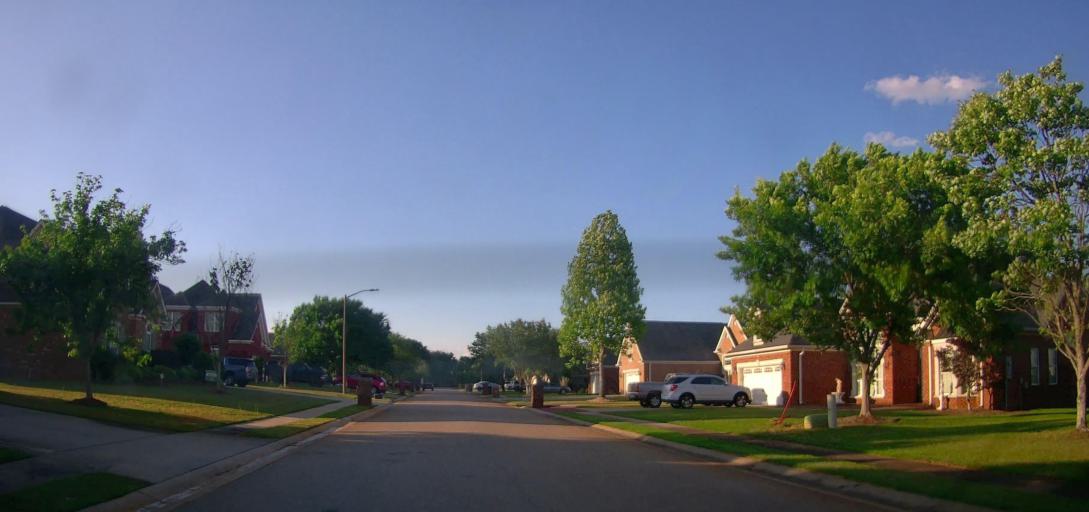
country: US
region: Georgia
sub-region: Houston County
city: Centerville
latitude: 32.6332
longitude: -83.7191
